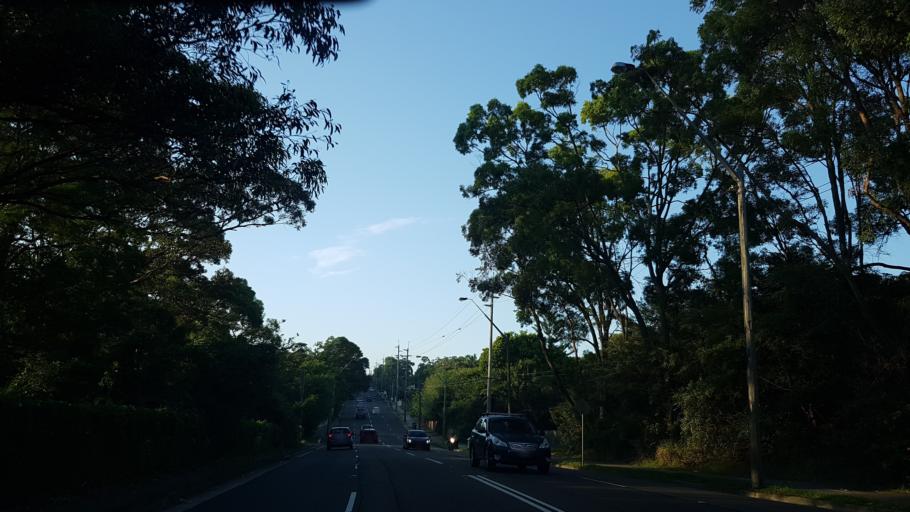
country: AU
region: New South Wales
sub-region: Warringah
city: Narraweena
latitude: -33.7483
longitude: 151.2621
